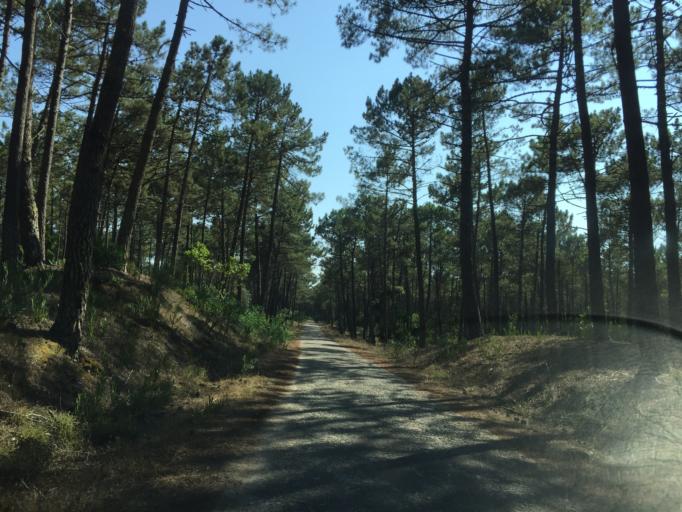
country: PT
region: Coimbra
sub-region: Figueira da Foz
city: Tavarede
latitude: 40.2513
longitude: -8.8414
